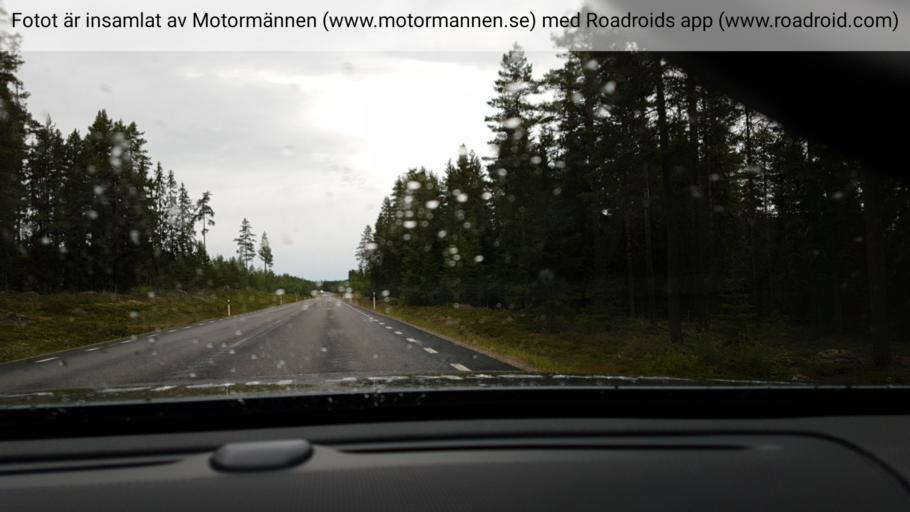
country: SE
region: Dalarna
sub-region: Rattviks Kommun
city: Raettvik
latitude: 60.8094
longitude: 15.2616
